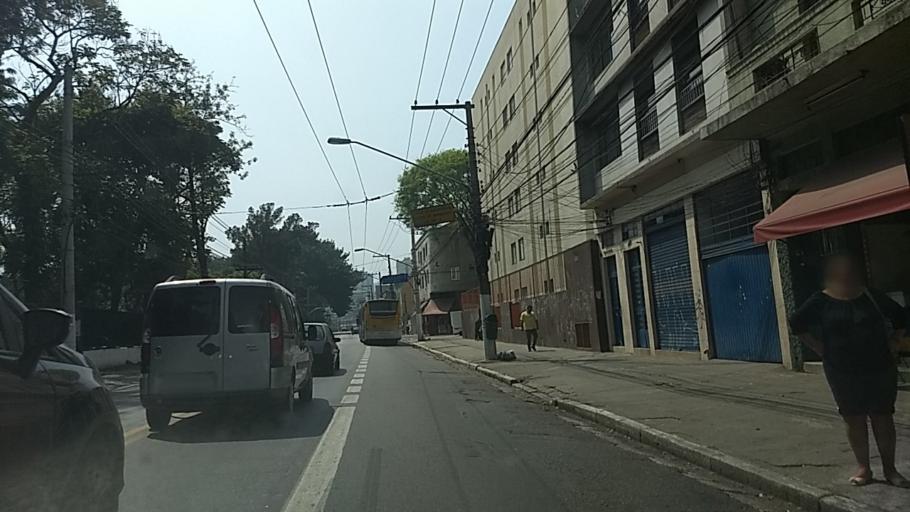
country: BR
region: Sao Paulo
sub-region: Sao Paulo
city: Sao Paulo
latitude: -23.5364
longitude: -46.5875
